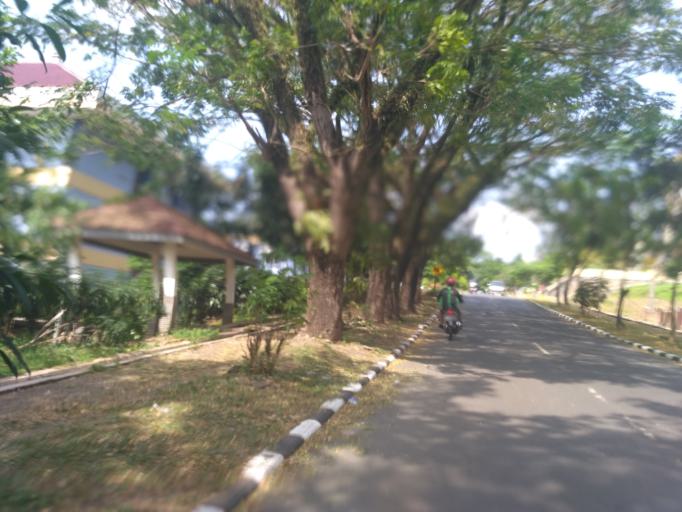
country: ID
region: Central Java
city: Semarang
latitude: -7.0505
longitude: 110.4421
